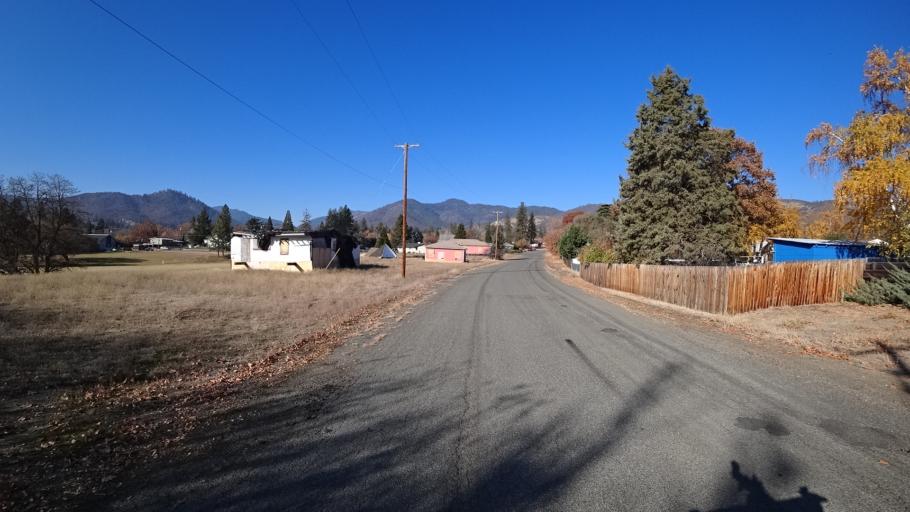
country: US
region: California
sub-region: Siskiyou County
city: Yreka
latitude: 41.7368
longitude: -122.6404
